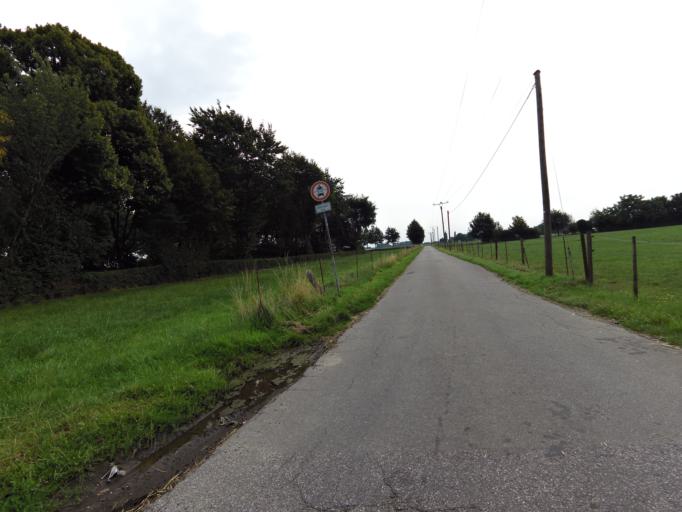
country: DE
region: North Rhine-Westphalia
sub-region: Regierungsbezirk Koln
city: Heinsberg
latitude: 51.0183
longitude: 6.0756
